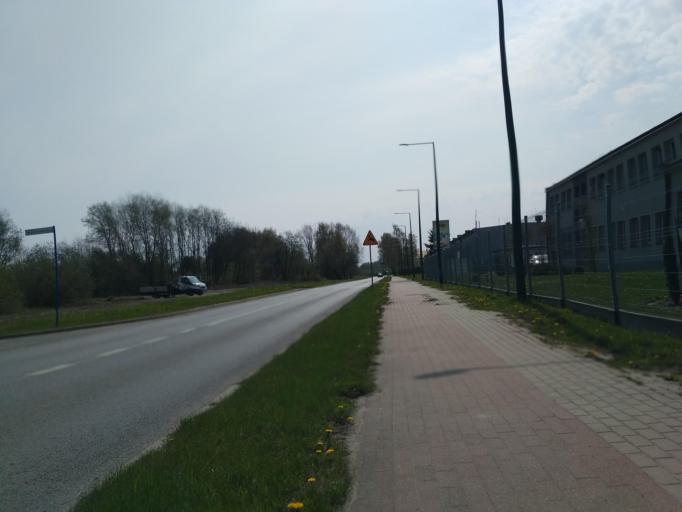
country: PL
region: Subcarpathian Voivodeship
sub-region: Krosno
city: Krosno
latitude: 49.6791
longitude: 21.7249
